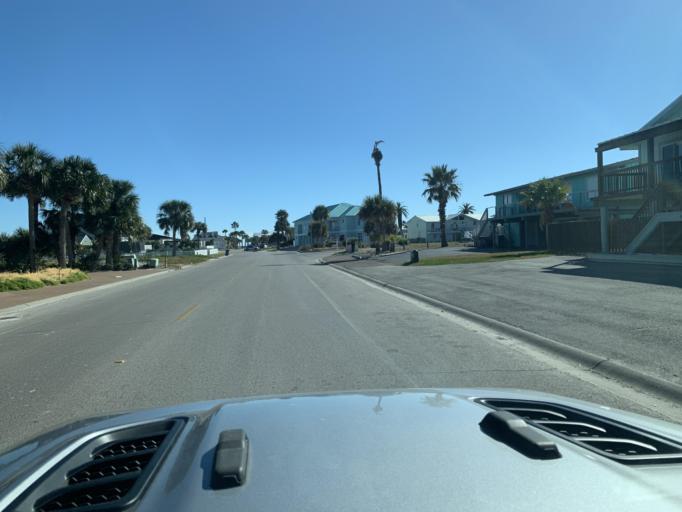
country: US
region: Texas
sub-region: Aransas County
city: Fulton
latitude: 28.0402
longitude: -97.0260
